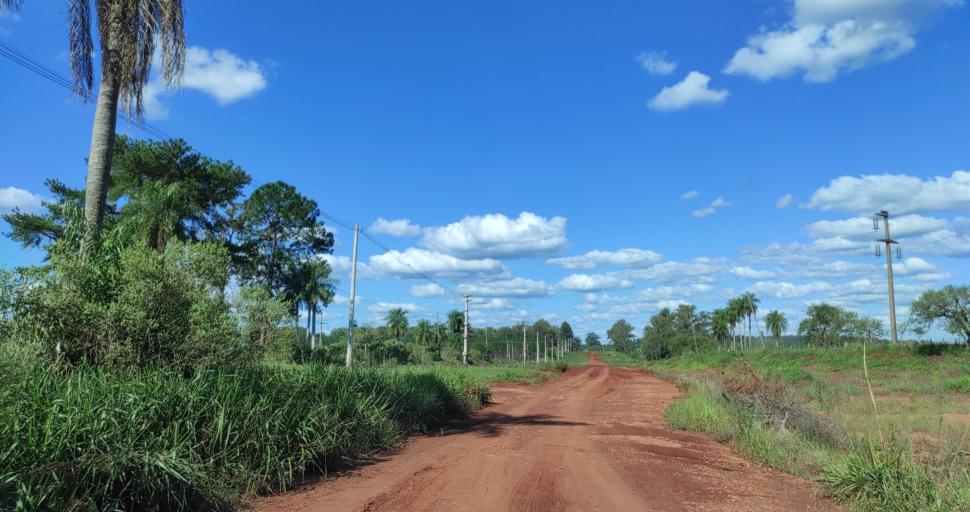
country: AR
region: Misiones
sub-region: Departamento de Candelaria
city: Candelaria
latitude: -27.4641
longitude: -55.7202
